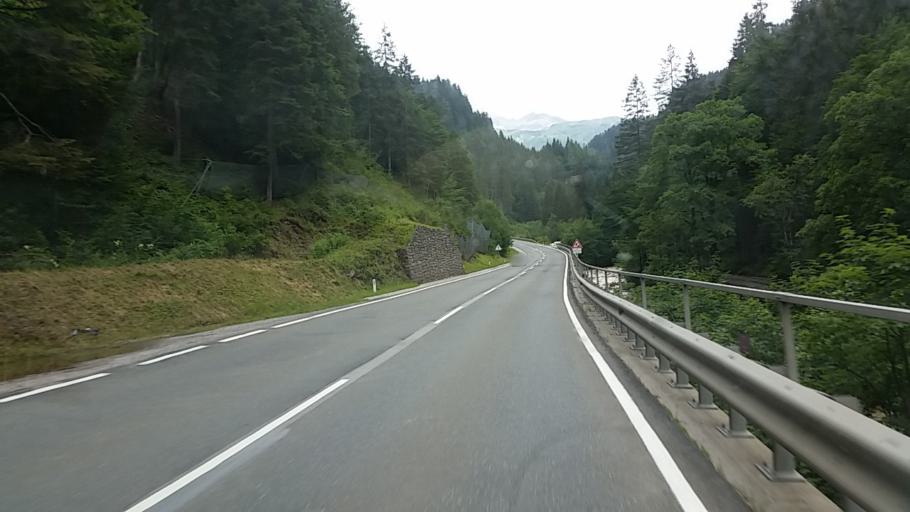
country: AT
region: Salzburg
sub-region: Politischer Bezirk Sankt Johann im Pongau
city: Untertauern
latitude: 47.2843
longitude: 13.5060
